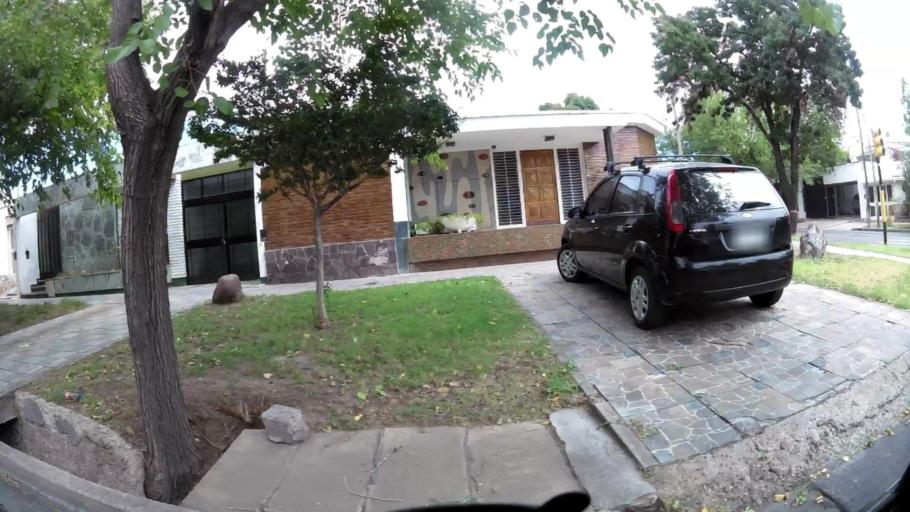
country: AR
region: Mendoza
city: Las Heras
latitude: -32.8722
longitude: -68.8552
